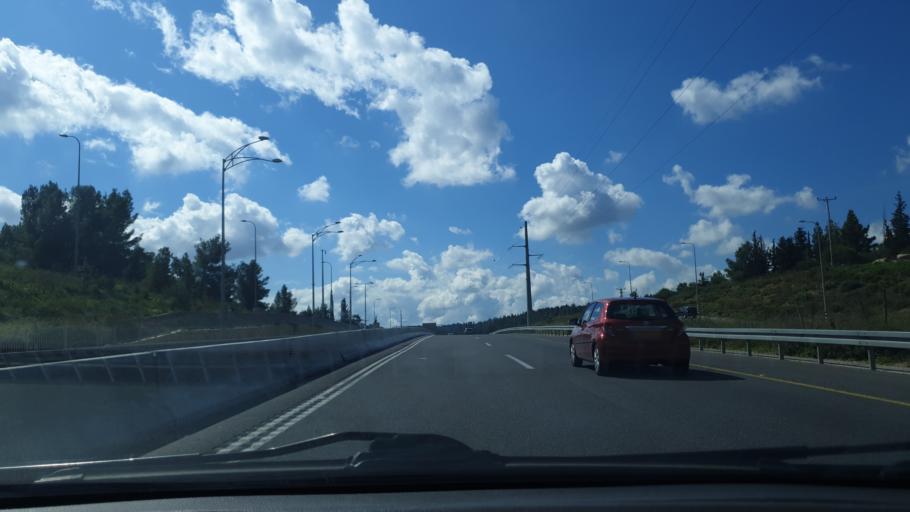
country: IL
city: Mevo horon
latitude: 31.8134
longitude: 35.0218
